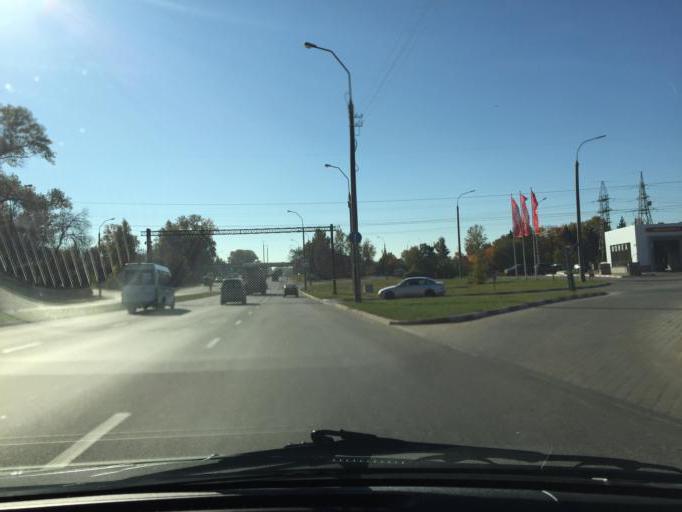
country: BY
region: Minsk
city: Syenitsa
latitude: 53.8390
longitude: 27.5330
